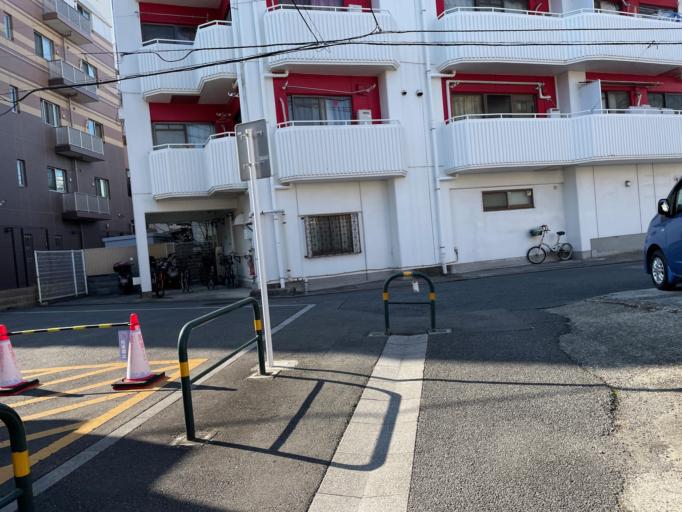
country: JP
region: Saitama
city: Soka
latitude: 35.7771
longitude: 139.7775
